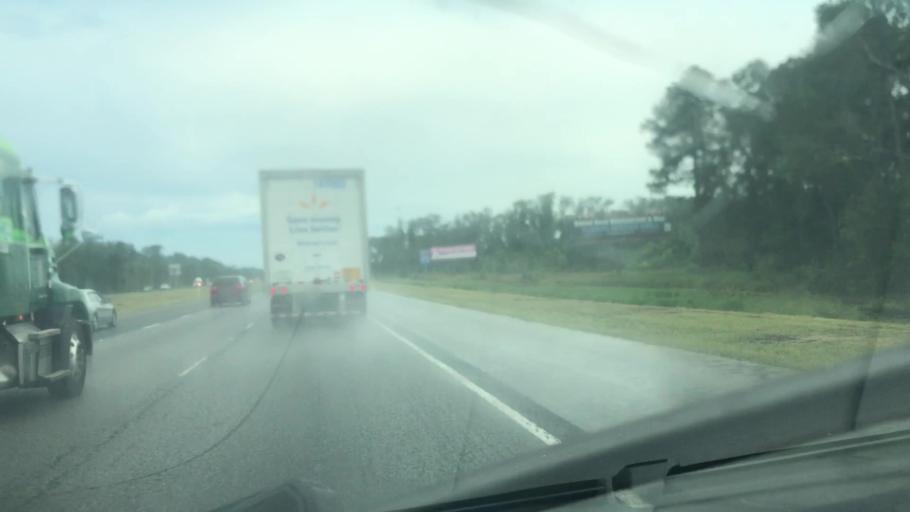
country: US
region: Georgia
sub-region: Camden County
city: Kingsland
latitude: 30.7863
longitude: -81.6580
